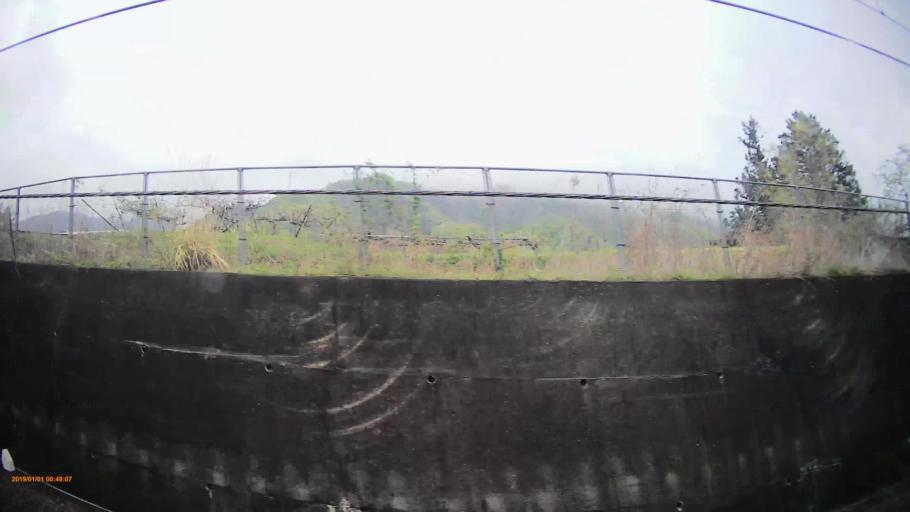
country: JP
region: Yamanashi
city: Otsuki
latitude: 35.6008
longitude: 138.9204
